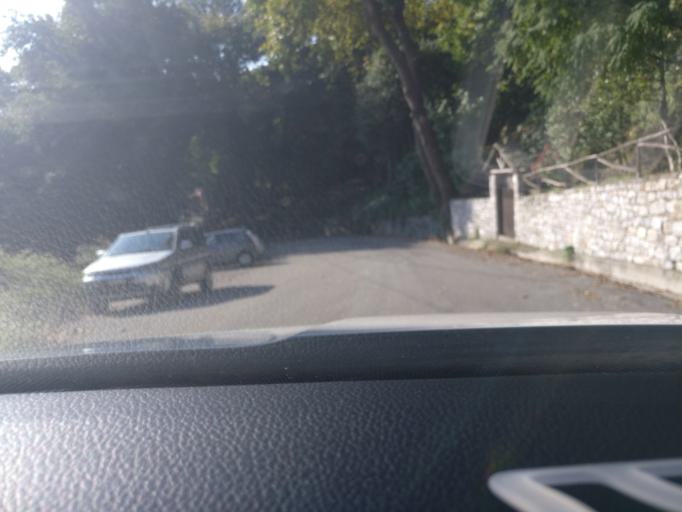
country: GR
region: Thessaly
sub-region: Nomos Magnisias
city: Zagora
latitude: 39.3841
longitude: 23.1806
